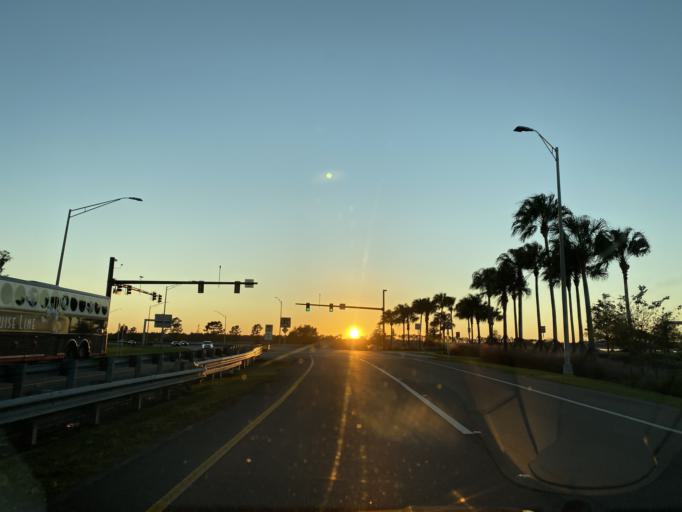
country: US
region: Florida
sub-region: Orange County
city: Taft
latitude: 28.4085
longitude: -81.3058
